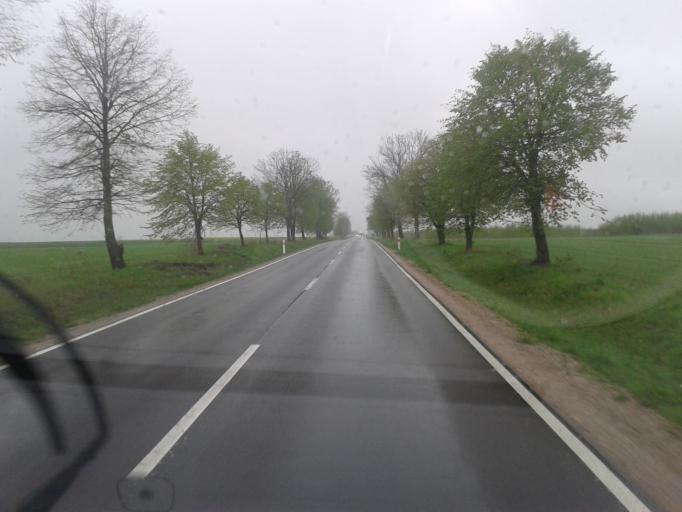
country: PL
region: Subcarpathian Voivodeship
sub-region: Powiat lubaczowski
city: Cieszanow
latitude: 50.2601
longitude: 23.1432
